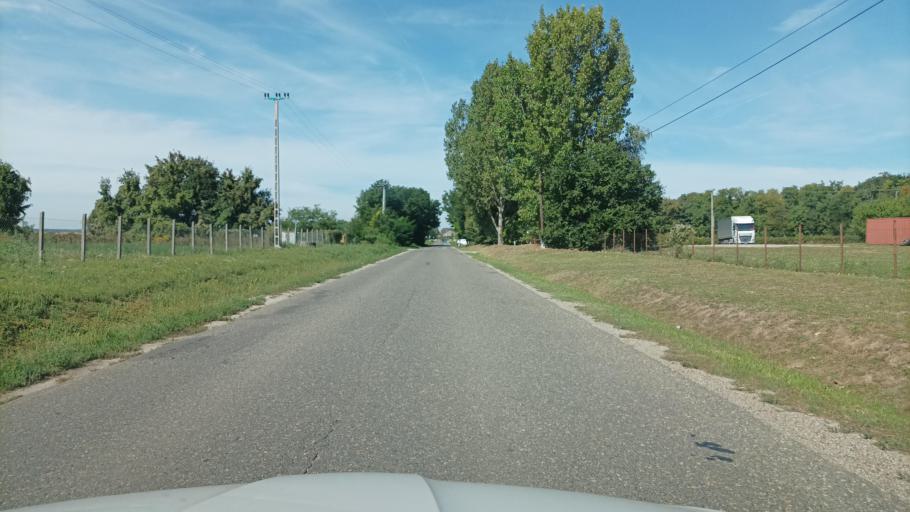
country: HU
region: Pest
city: Vacszentlaszlo
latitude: 47.5663
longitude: 19.5474
